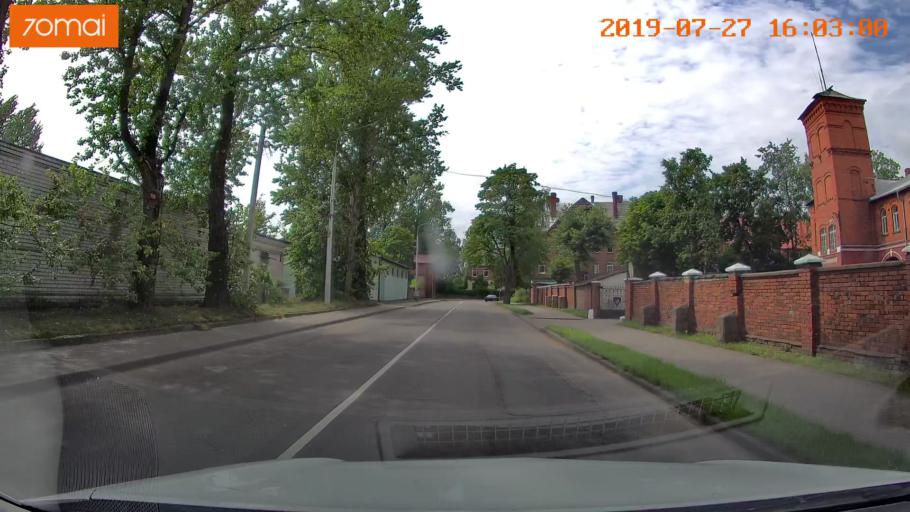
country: RU
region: Kaliningrad
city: Chernyakhovsk
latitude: 54.6308
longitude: 21.8049
